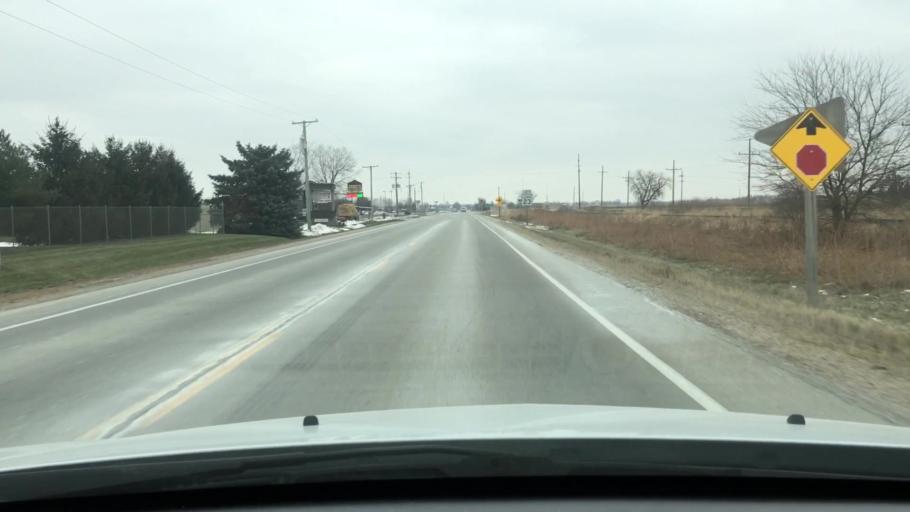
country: US
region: Illinois
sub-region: DeKalb County
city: Waterman
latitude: 41.7692
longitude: -88.7587
